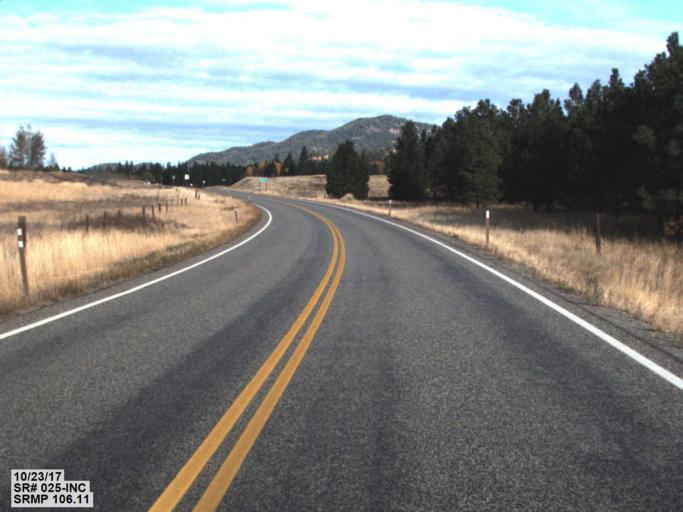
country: CA
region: British Columbia
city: Rossland
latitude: 48.8513
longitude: -117.8877
